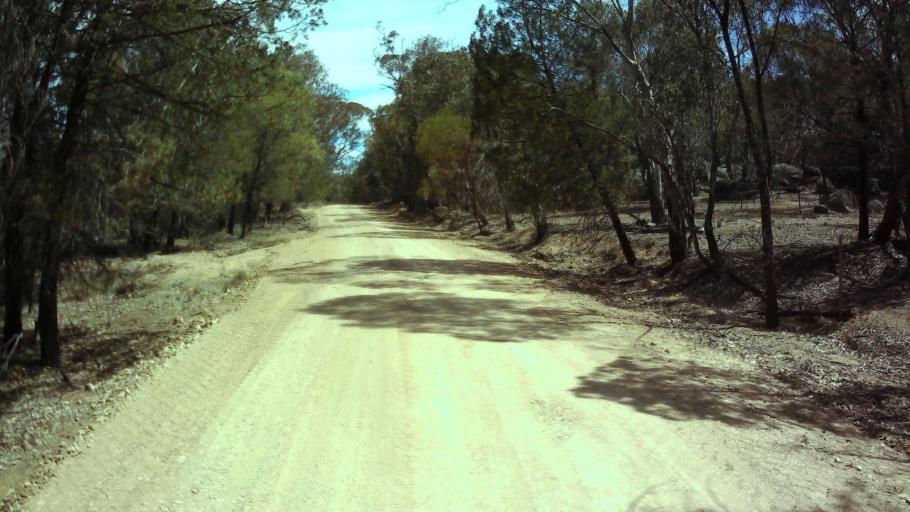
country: AU
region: New South Wales
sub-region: Weddin
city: Grenfell
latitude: -33.8079
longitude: 148.1598
